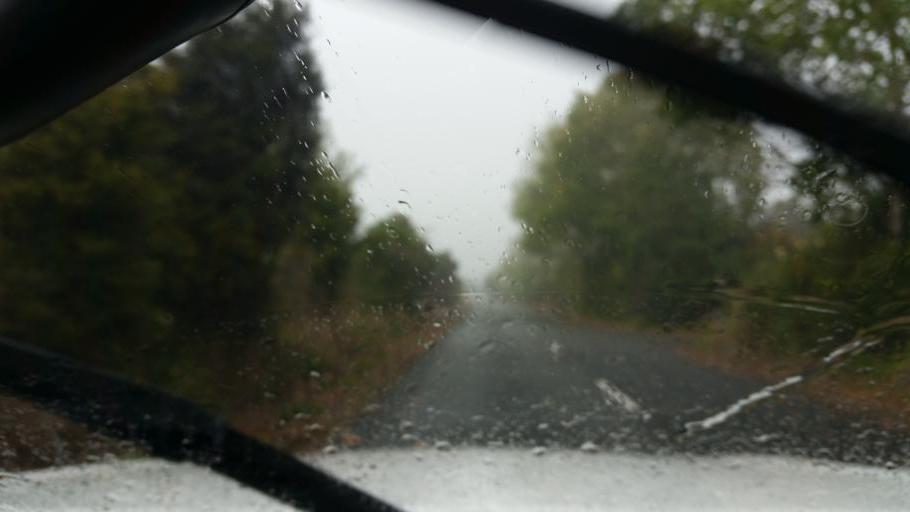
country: NZ
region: Auckland
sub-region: Auckland
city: Wellsford
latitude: -36.0881
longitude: 174.5551
